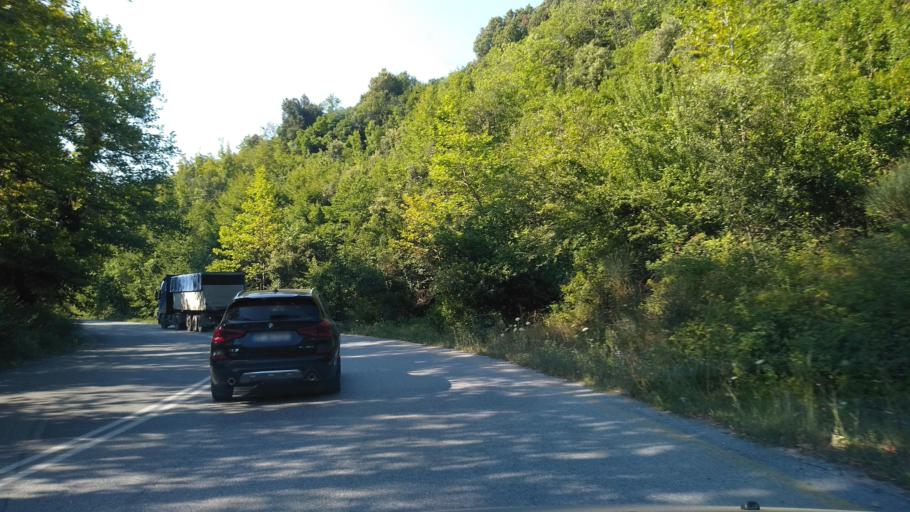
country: GR
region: Central Macedonia
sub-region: Nomos Chalkidikis
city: Stratonion
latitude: 40.5292
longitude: 23.8232
